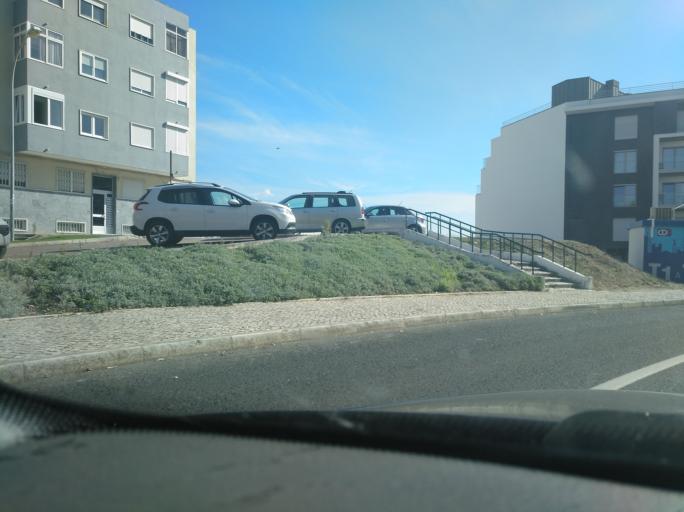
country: PT
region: Lisbon
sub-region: Oeiras
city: Alges
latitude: 38.7042
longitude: -9.2321
